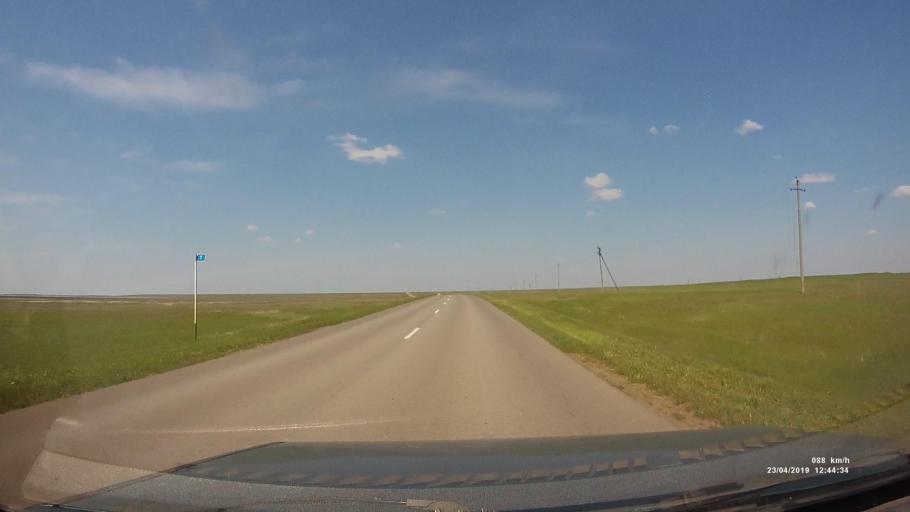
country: RU
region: Kalmykiya
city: Yashalta
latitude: 46.4785
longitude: 42.6468
